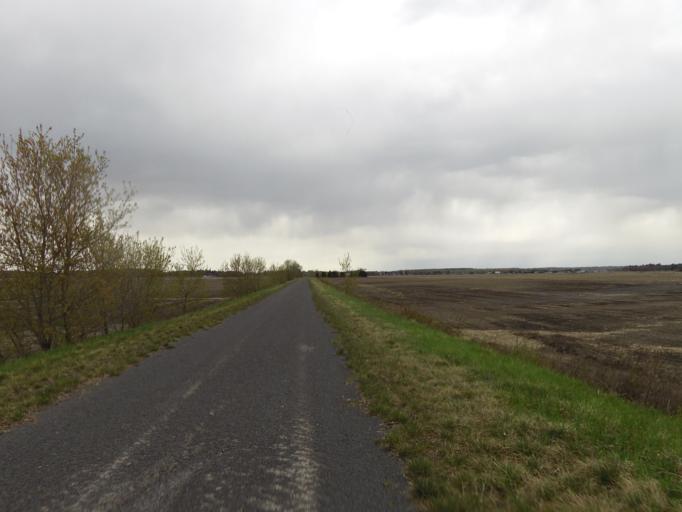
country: CA
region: Ontario
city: Bourget
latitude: 45.4480
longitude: -75.1194
